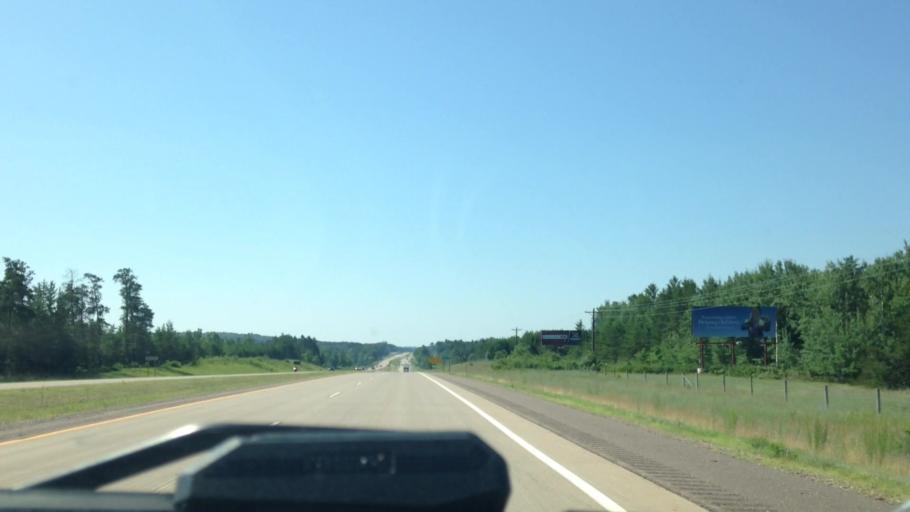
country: US
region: Wisconsin
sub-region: Washburn County
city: Spooner
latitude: 45.9196
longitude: -91.8282
